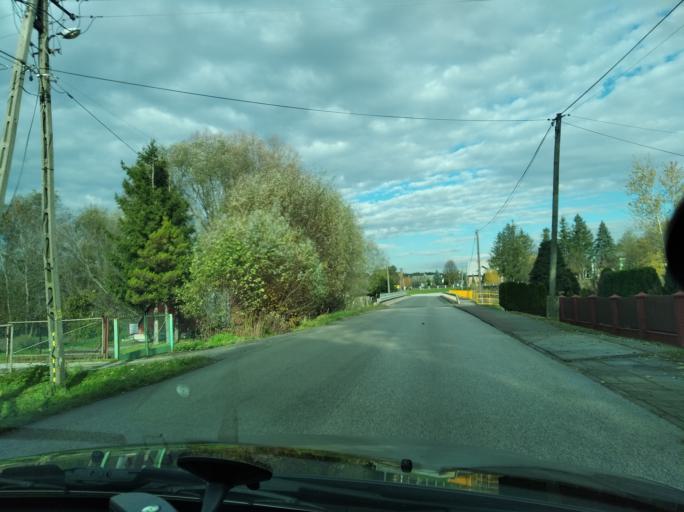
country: PL
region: Subcarpathian Voivodeship
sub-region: Powiat debicki
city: Brzeznica
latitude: 50.0899
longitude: 21.5216
